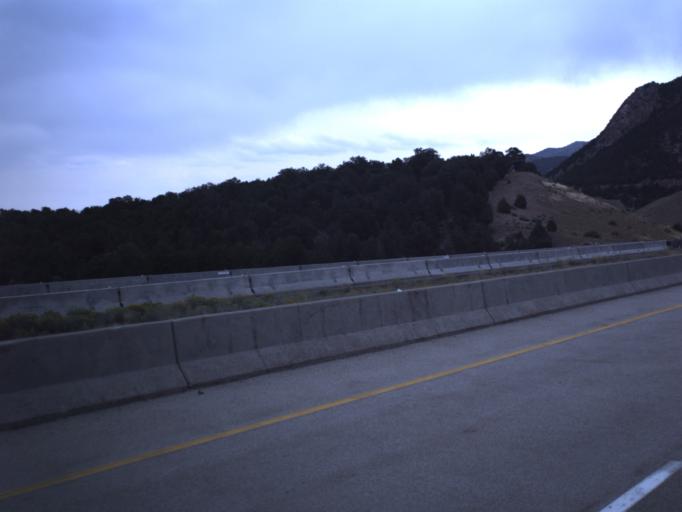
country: US
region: Utah
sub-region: Sevier County
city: Monroe
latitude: 38.5476
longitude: -112.3799
